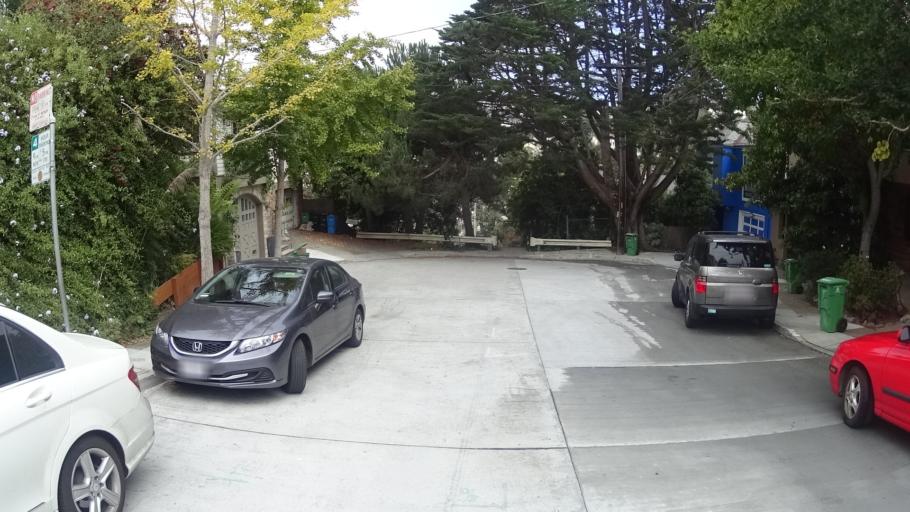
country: US
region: California
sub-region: San Mateo County
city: Daly City
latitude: 37.7336
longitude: -122.4377
